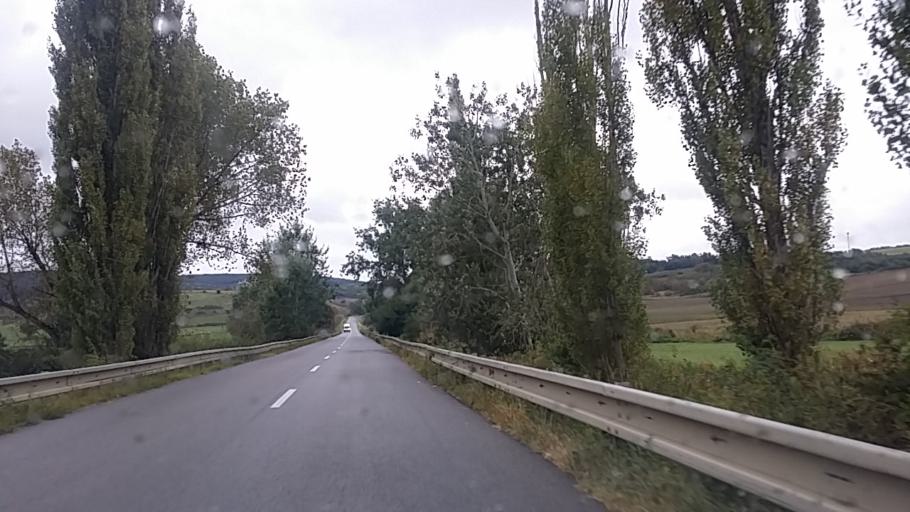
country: HU
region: Komarom-Esztergom
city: Esztergom
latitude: 47.8730
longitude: 18.7525
